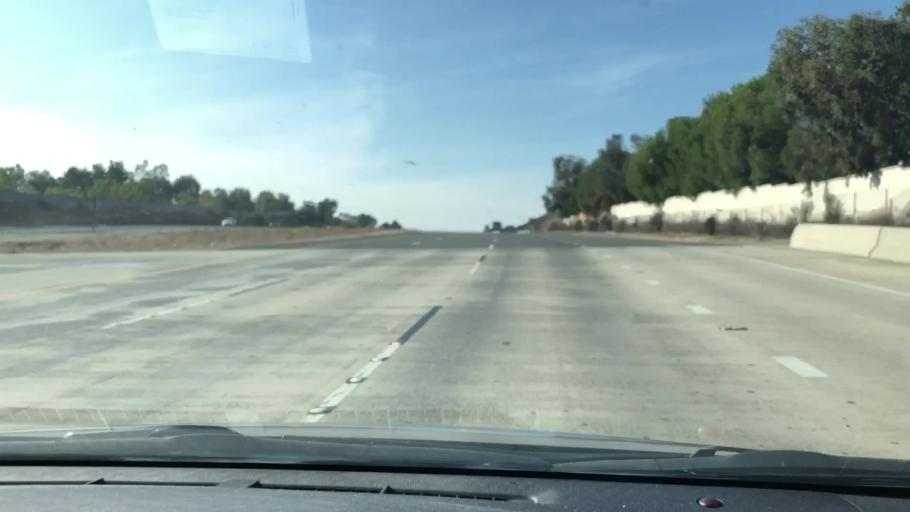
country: US
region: California
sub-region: Orange County
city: Rancho Santa Margarita
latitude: 33.6520
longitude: -117.6123
